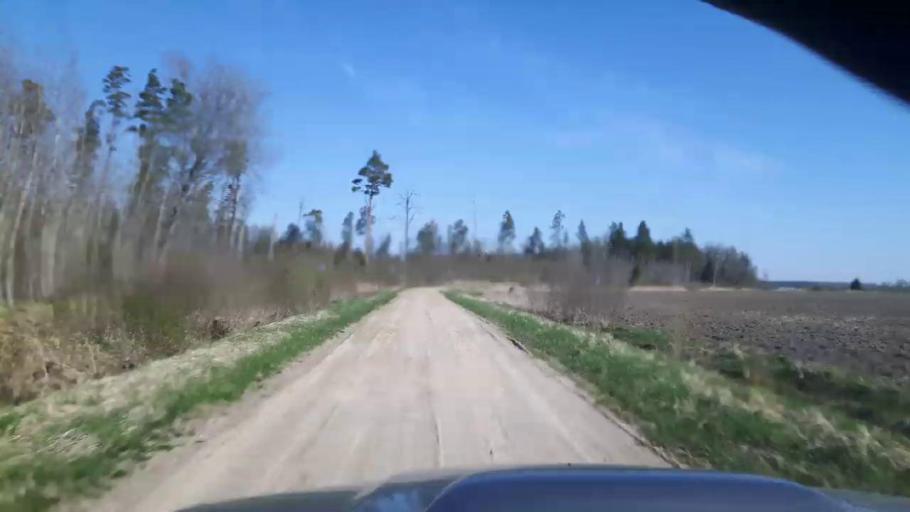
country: EE
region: Paernumaa
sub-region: Vaendra vald (alev)
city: Vandra
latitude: 58.5245
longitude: 24.9597
